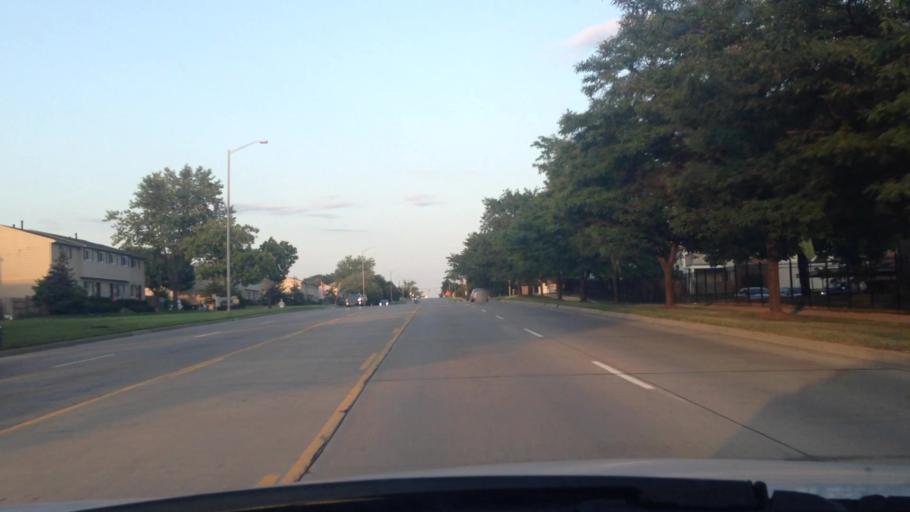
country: US
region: Michigan
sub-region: Oakland County
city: Auburn Hills
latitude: 42.6780
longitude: -83.2594
